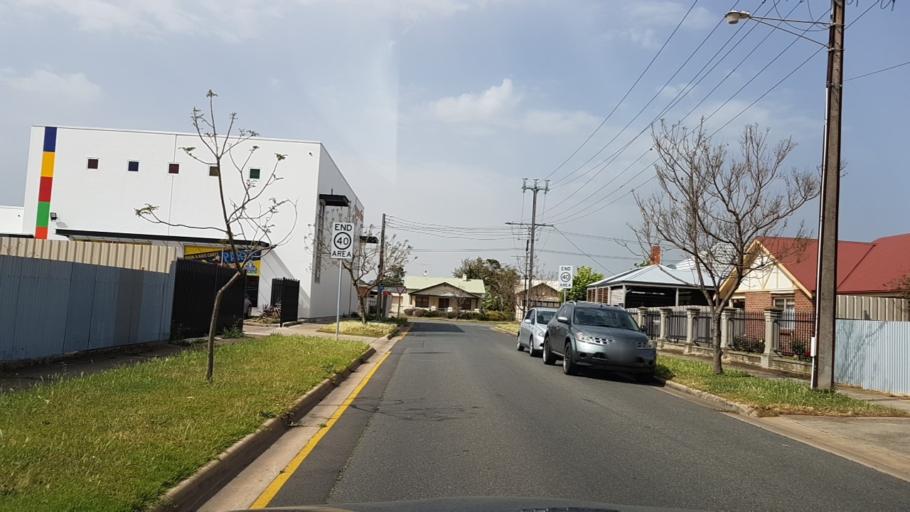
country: AU
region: South Australia
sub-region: Charles Sturt
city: Seaton
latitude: -34.8909
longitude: 138.5198
